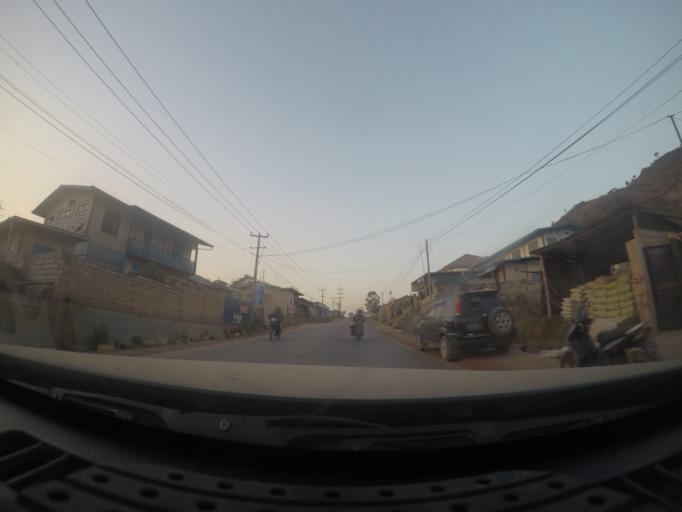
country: MM
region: Shan
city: Taunggyi
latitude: 20.7430
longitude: 97.0508
